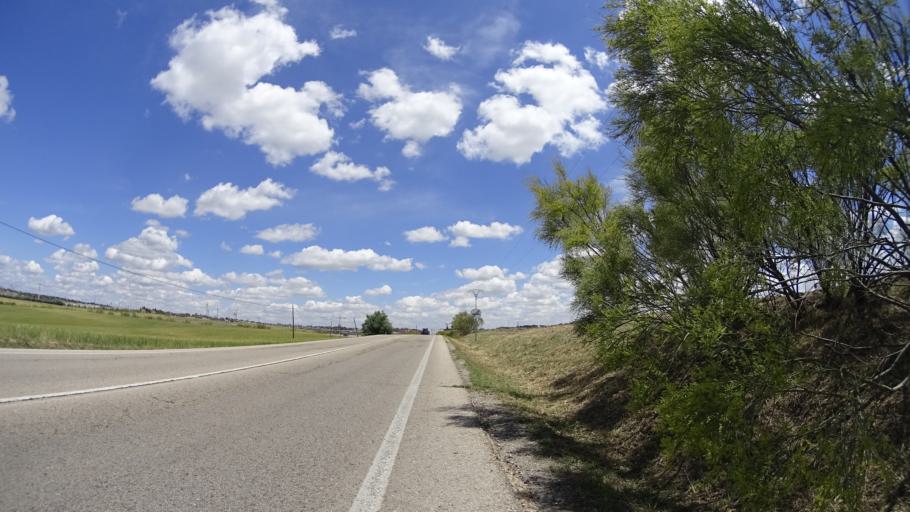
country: ES
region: Madrid
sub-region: Provincia de Madrid
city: Boadilla del Monte
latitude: 40.4119
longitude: -3.9276
